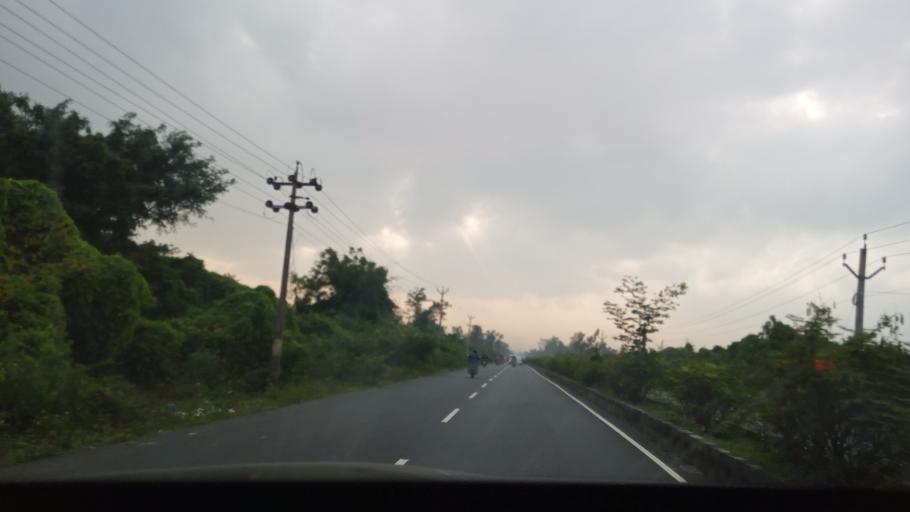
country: IN
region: Tamil Nadu
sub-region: Kancheepuram
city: Vengavasal
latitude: 12.8216
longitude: 80.1717
